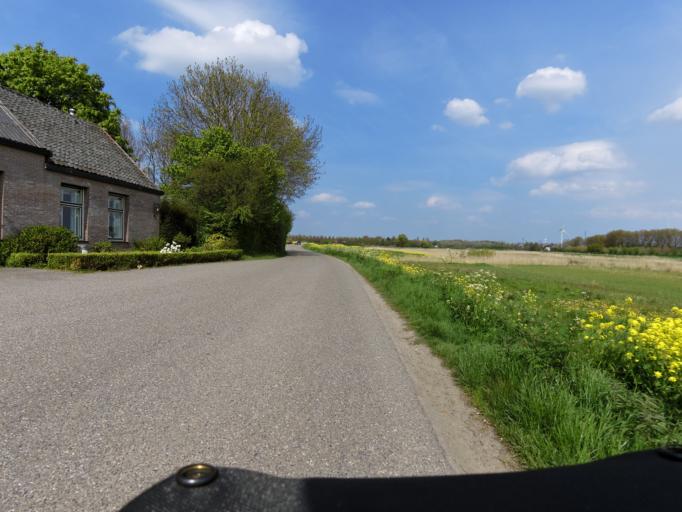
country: NL
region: South Holland
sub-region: Gemeente Brielle
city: Brielle
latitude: 51.8745
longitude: 4.2099
